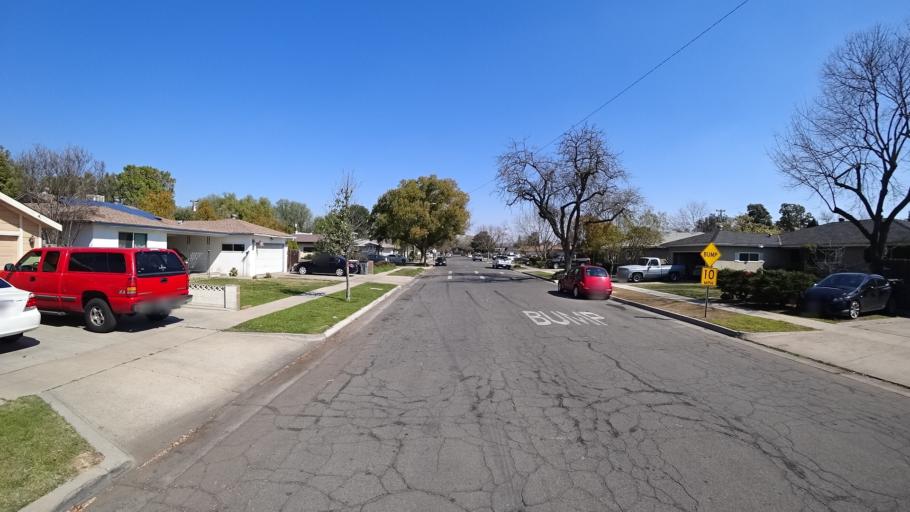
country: US
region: California
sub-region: Fresno County
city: Tarpey Village
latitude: 36.8046
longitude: -119.7357
